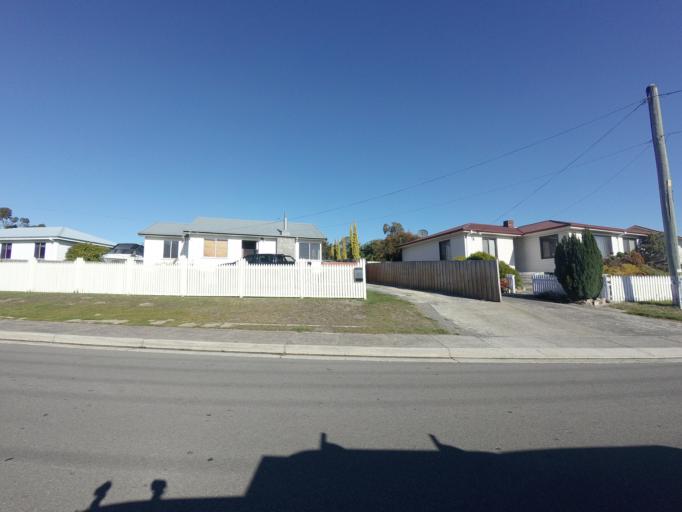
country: AU
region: Tasmania
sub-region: Clarence
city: Warrane
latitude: -42.8556
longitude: 147.3882
